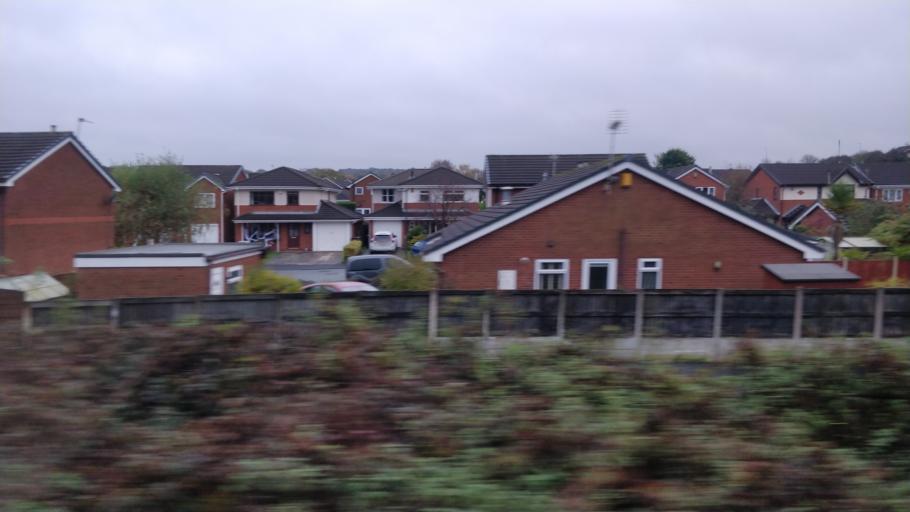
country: GB
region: England
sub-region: Lancashire
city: Appley Bridge
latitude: 53.5758
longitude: -2.7144
